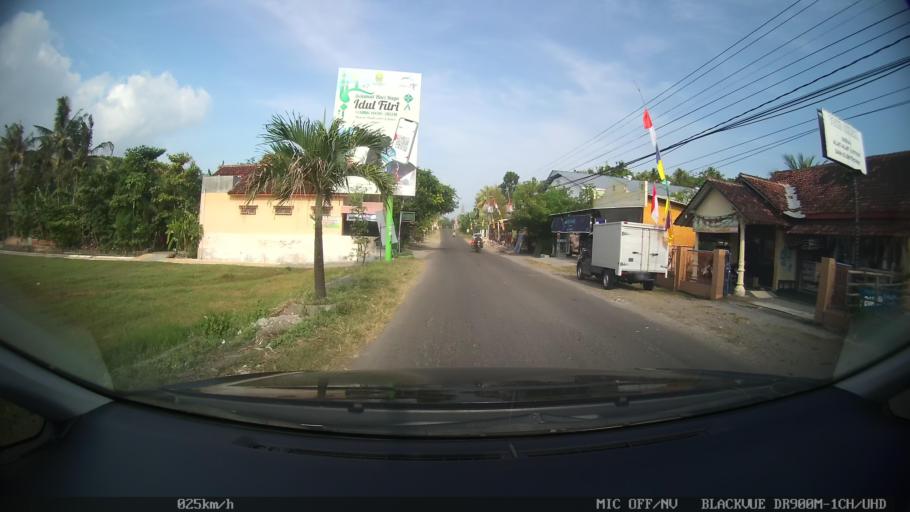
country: ID
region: Daerah Istimewa Yogyakarta
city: Kasihan
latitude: -7.8497
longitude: 110.3151
